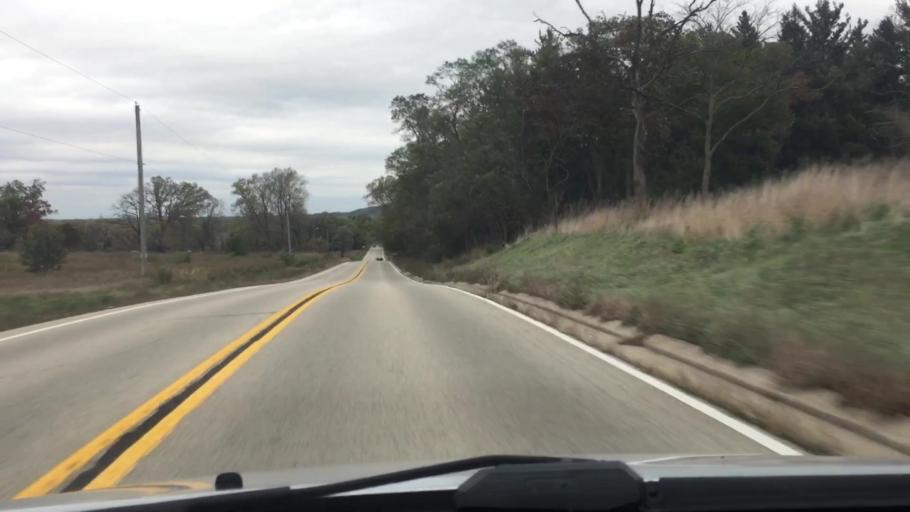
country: US
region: Wisconsin
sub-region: Waukesha County
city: Eagle
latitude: 42.9100
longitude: -88.4738
